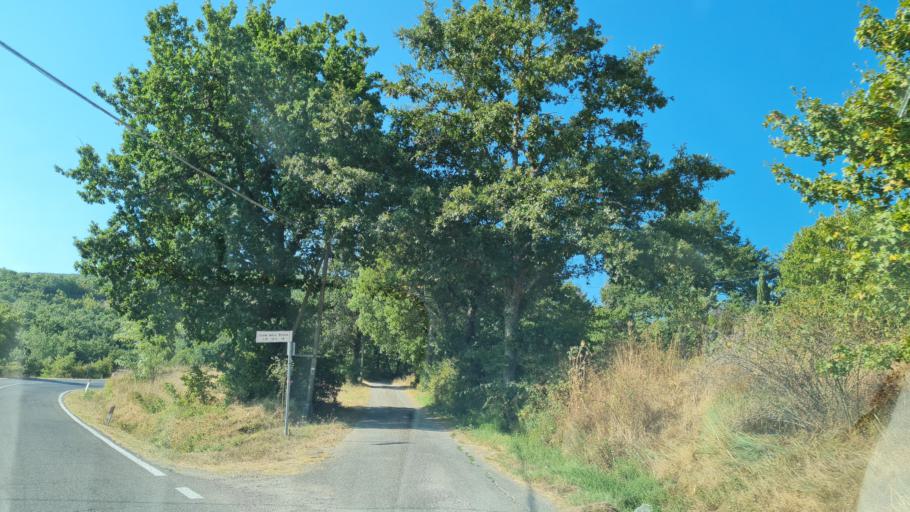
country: IT
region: Tuscany
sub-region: Provincia di Siena
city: Chianciano Terme
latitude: 43.0287
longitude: 11.7949
